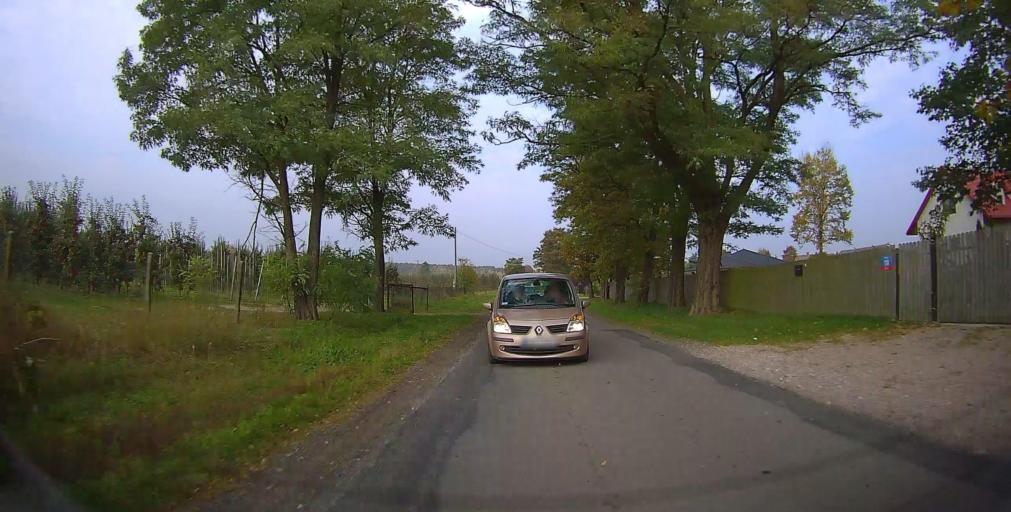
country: PL
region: Masovian Voivodeship
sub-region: Powiat grojecki
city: Mogielnica
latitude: 51.6557
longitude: 20.7191
